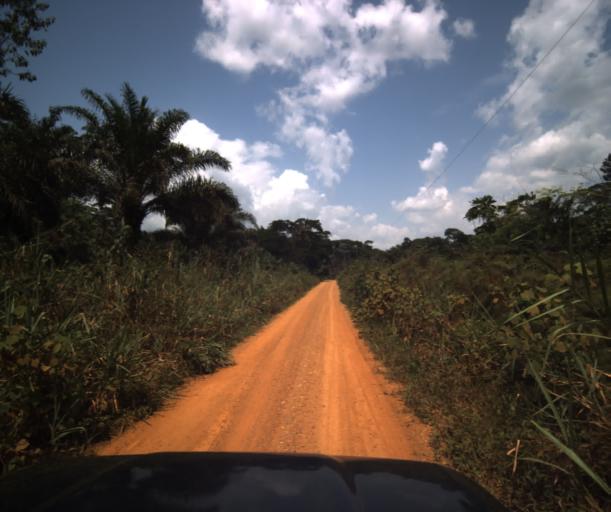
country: CM
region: Centre
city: Eseka
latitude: 3.5401
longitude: 11.0105
